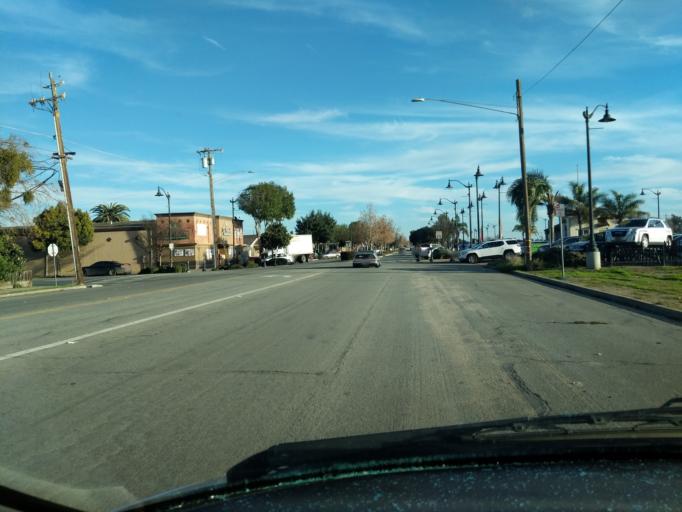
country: US
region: California
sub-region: Monterey County
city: Soledad
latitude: 36.4284
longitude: -121.3318
